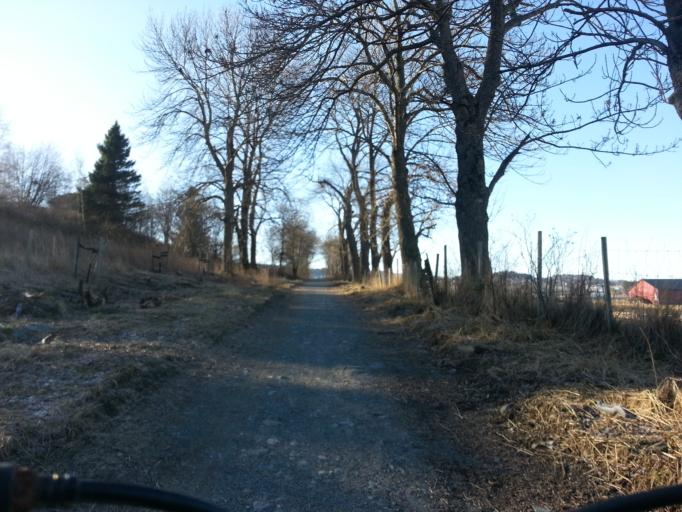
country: NO
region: Sor-Trondelag
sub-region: Trondheim
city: Trondheim
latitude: 63.4339
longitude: 10.4837
